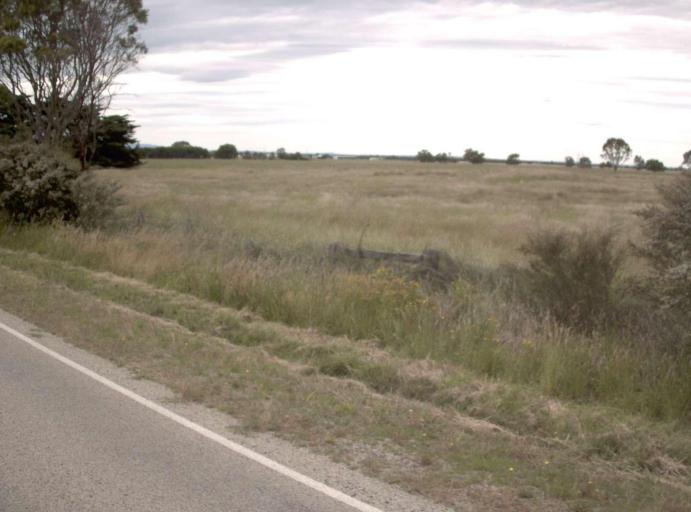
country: AU
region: Victoria
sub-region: East Gippsland
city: Bairnsdale
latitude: -37.8898
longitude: 147.5569
